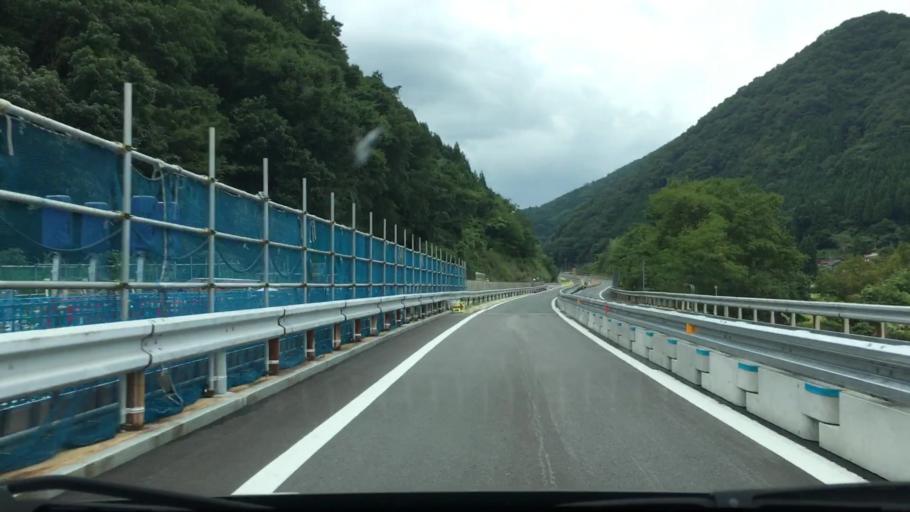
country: JP
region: Okayama
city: Niimi
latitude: 35.0036
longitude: 133.4039
